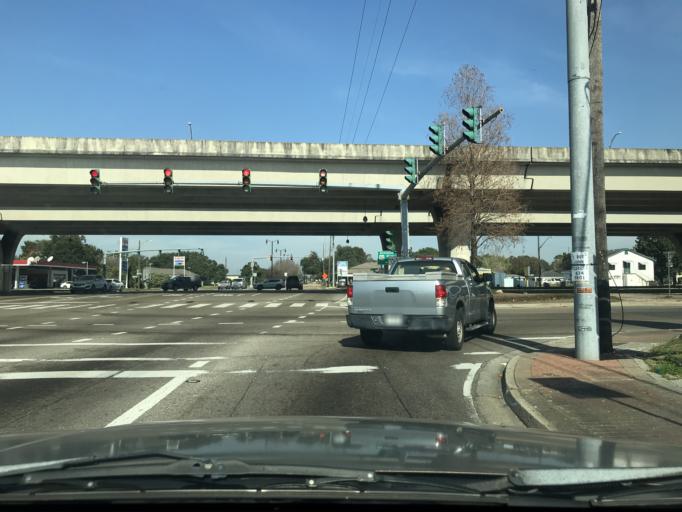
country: US
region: Louisiana
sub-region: Jefferson Parish
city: Marrero
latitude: 29.8941
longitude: -90.0999
